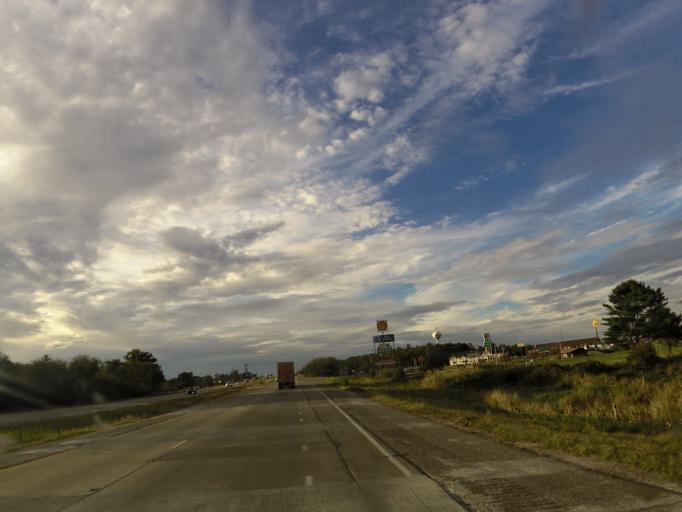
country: US
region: Wisconsin
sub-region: Juneau County
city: Mauston
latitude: 43.7932
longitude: -90.0534
